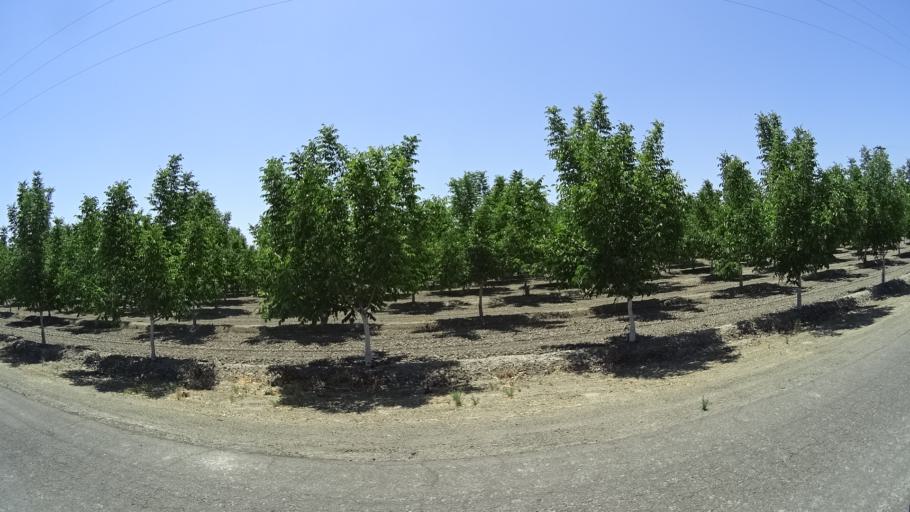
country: US
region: California
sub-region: Fresno County
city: Laton
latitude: 36.3864
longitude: -119.7349
